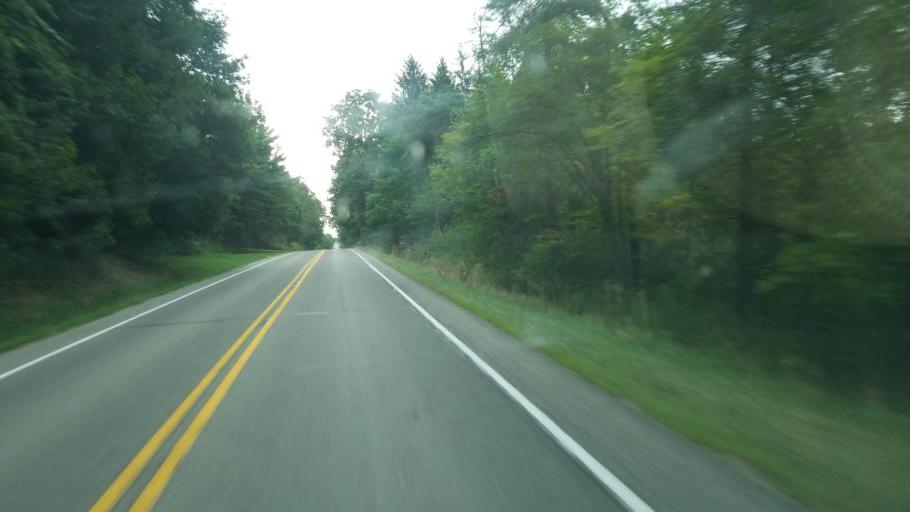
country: US
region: Pennsylvania
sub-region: Clarion County
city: Knox
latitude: 41.2093
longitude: -79.6540
